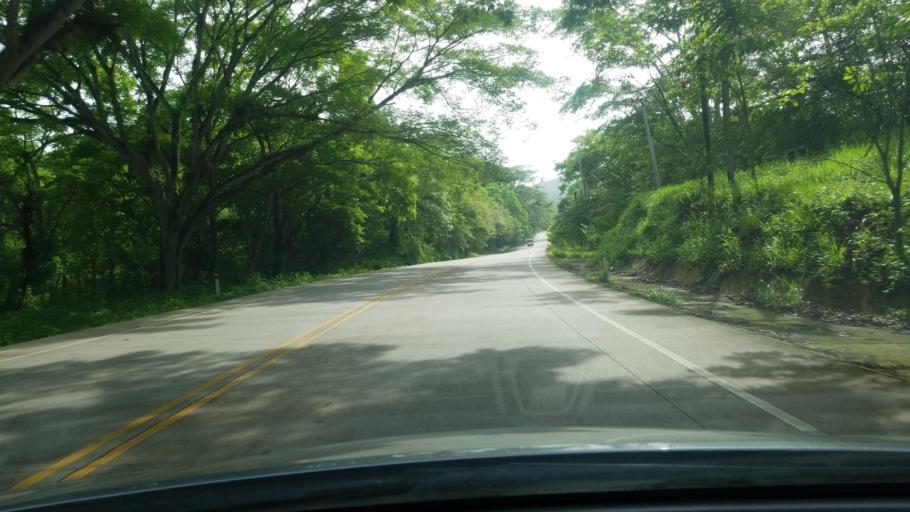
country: HN
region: Copan
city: Copan
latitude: 14.8430
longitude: -89.1420
